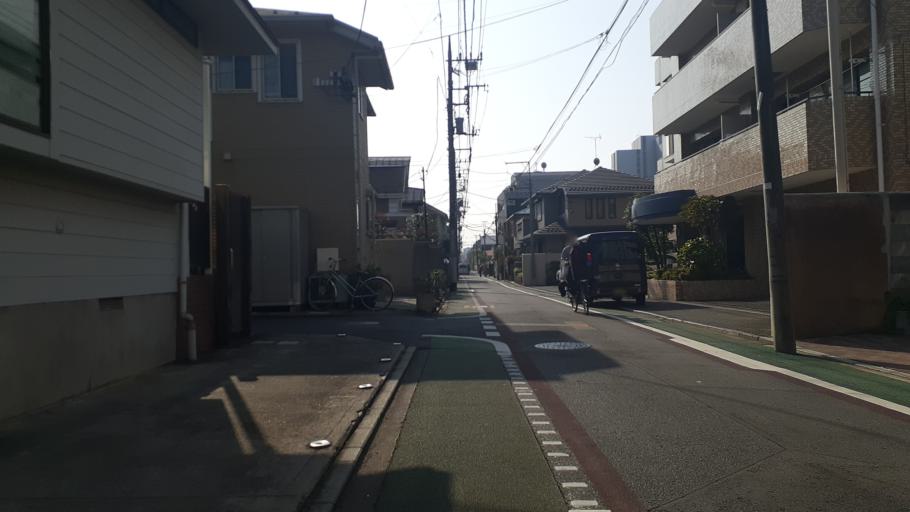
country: JP
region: Tokyo
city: Musashino
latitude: 35.7089
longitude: 139.5672
